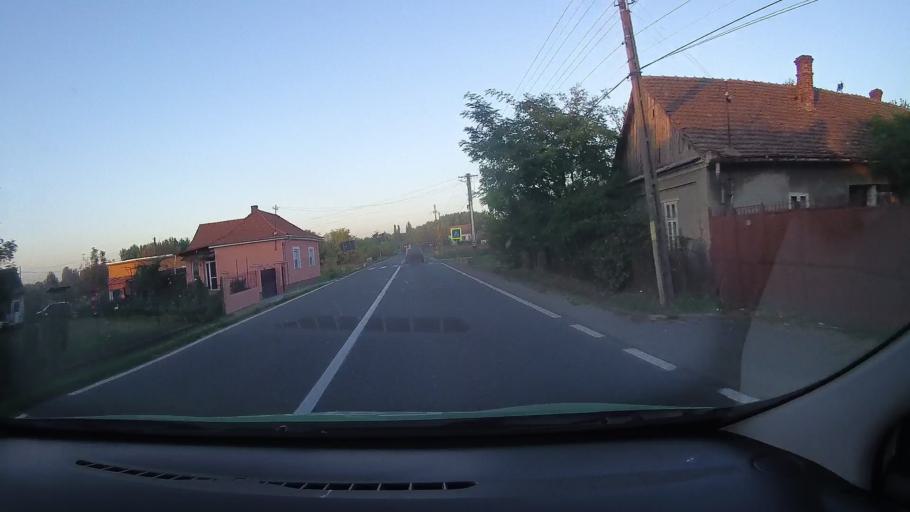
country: RO
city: Szekelyhid
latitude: 47.3385
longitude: 22.0913
